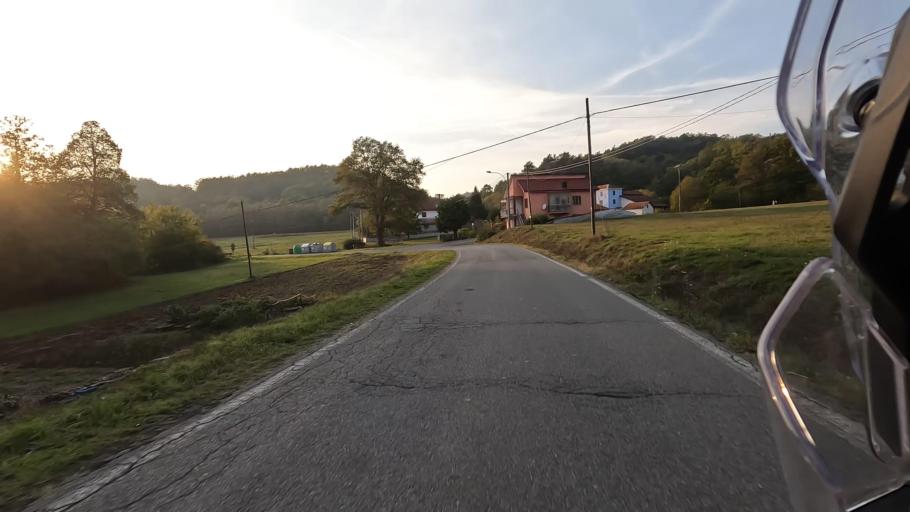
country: IT
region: Liguria
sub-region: Provincia di Savona
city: Mioglia
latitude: 44.5109
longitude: 8.4404
